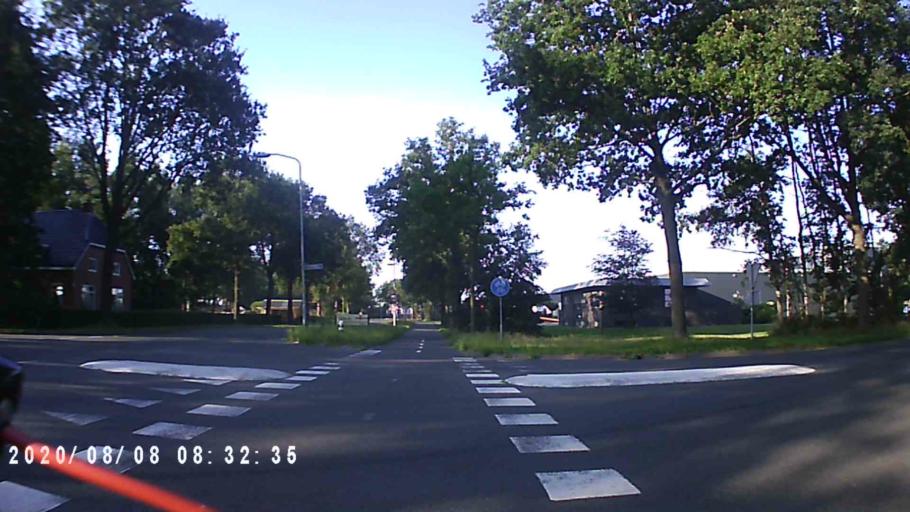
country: NL
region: Groningen
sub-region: Gemeente Leek
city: Leek
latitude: 53.0754
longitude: 6.3326
